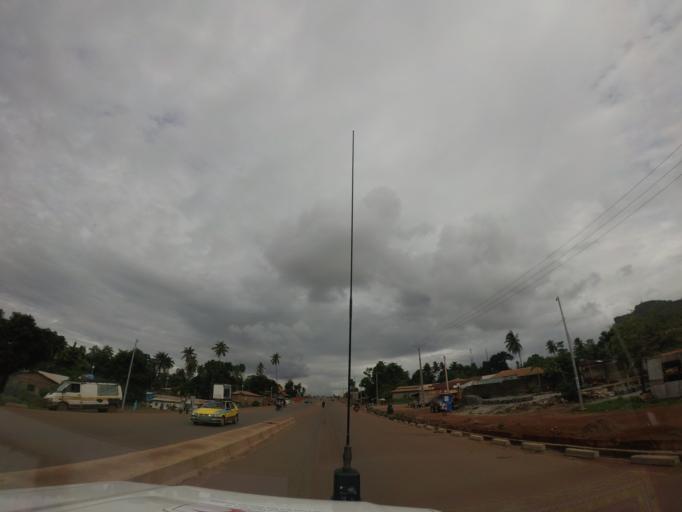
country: GN
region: Kindia
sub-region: Coyah
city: Coyah
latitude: 9.7075
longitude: -13.3886
